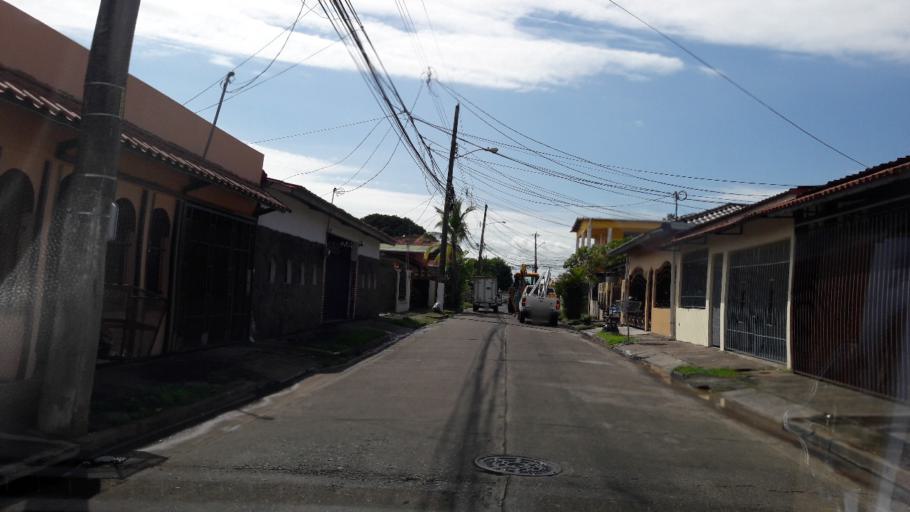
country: PA
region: Panama
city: Tocumen
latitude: 9.0602
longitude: -79.4158
